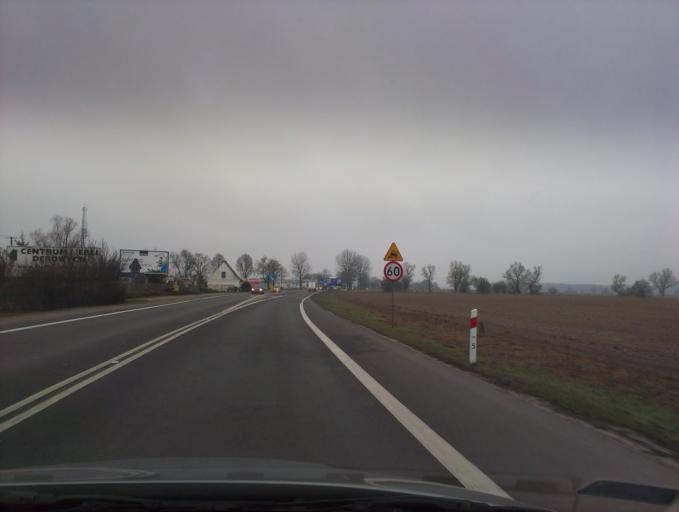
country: PL
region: Greater Poland Voivodeship
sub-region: Powiat pilski
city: Ujscie
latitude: 53.1004
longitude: 16.7466
